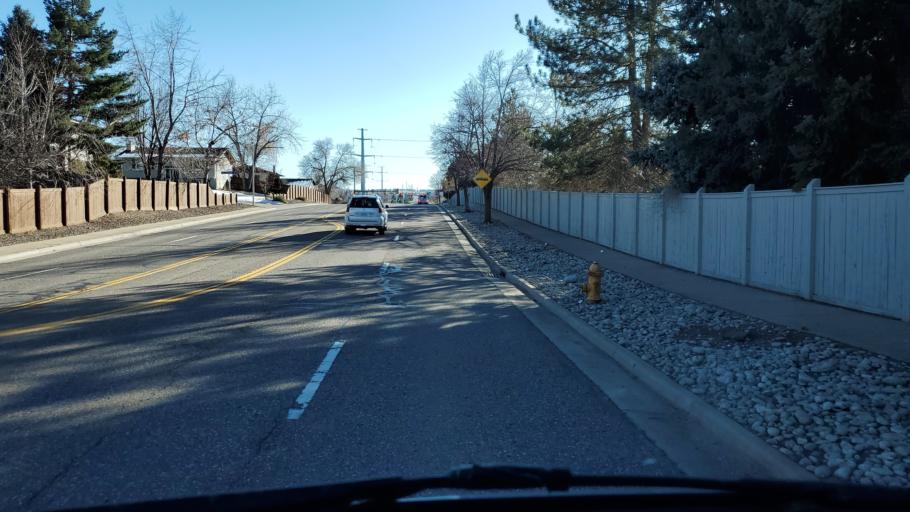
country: US
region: Colorado
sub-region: Arapahoe County
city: Castlewood
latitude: 39.5825
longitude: -104.9043
